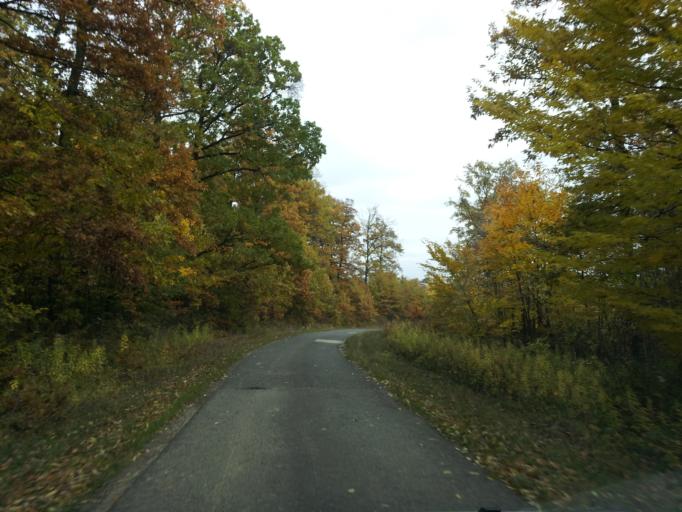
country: HU
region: Gyor-Moson-Sopron
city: Pannonhalma
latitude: 47.4947
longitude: 17.7261
